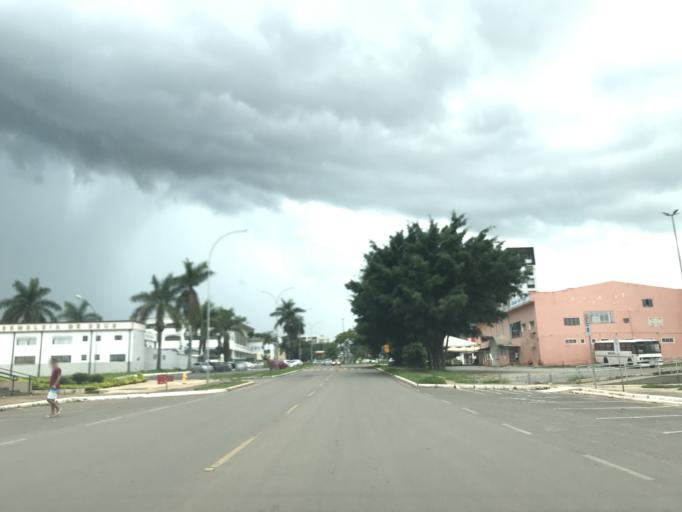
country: BR
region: Federal District
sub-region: Brasilia
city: Brasilia
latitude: -15.6473
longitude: -47.8050
